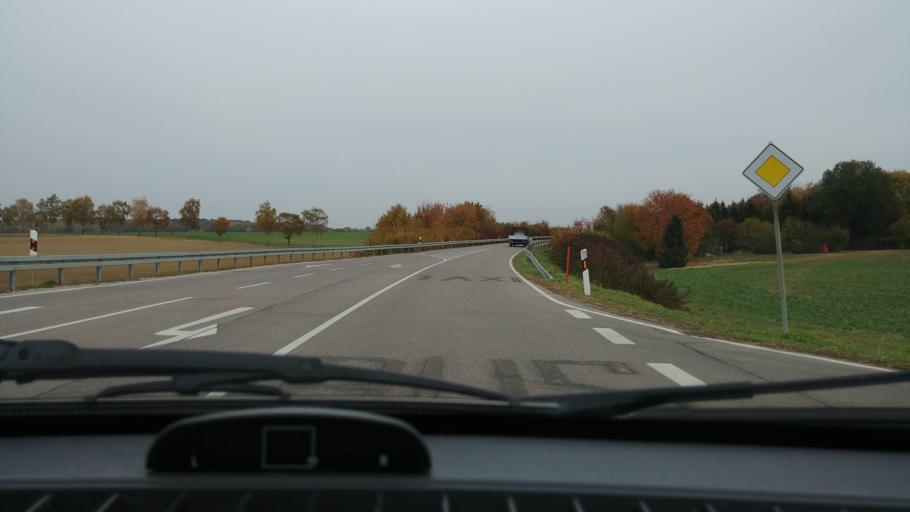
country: DE
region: Baden-Wuerttemberg
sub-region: Regierungsbezirk Stuttgart
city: Rot am See
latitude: 49.2530
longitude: 10.0377
